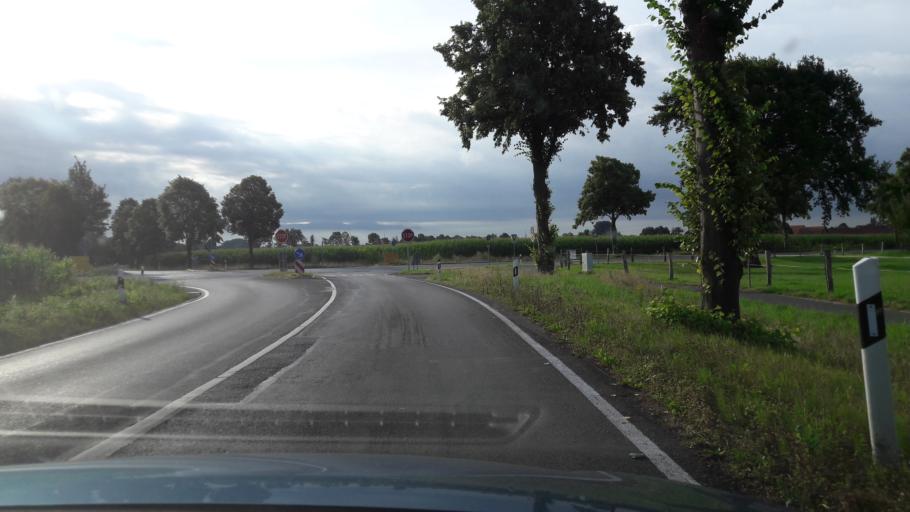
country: DE
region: North Rhine-Westphalia
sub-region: Regierungsbezirk Munster
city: Everswinkel
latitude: 51.8673
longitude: 7.9251
